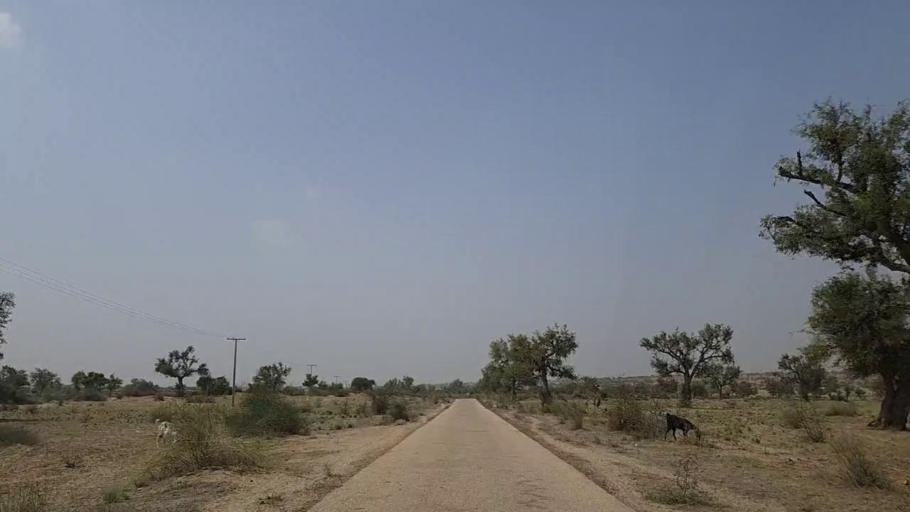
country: PK
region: Sindh
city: Mithi
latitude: 24.7636
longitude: 69.9167
